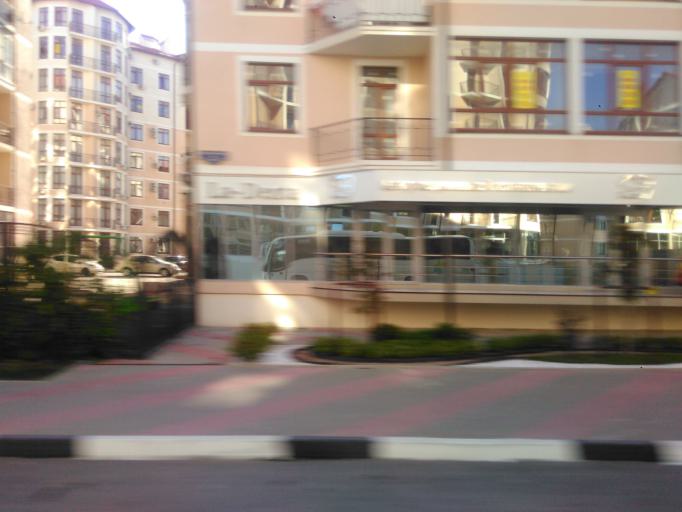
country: RU
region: Krasnodarskiy
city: Gelendzhik
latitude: 44.5492
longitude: 38.0605
